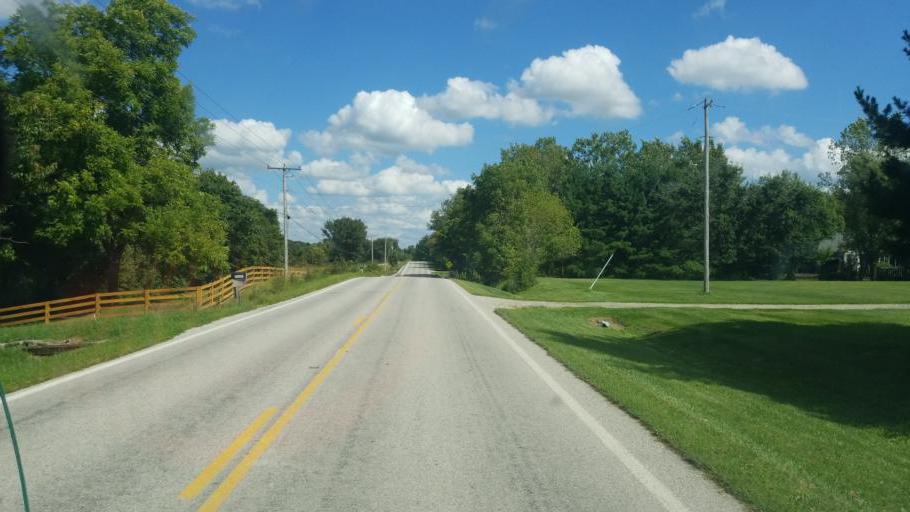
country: US
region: Ohio
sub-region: Delaware County
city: Delaware
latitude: 40.3220
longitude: -83.1849
